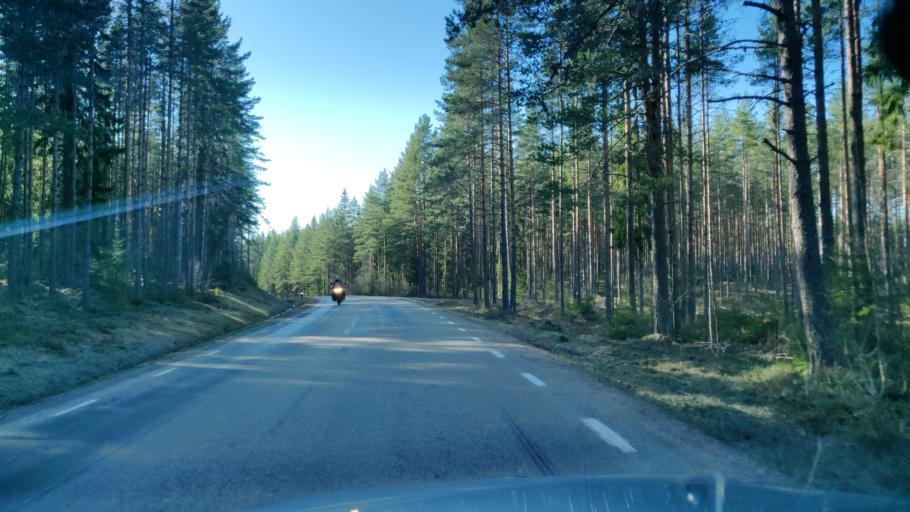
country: SE
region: Vaermland
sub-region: Sunne Kommun
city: Sunne
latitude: 59.9918
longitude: 13.3072
